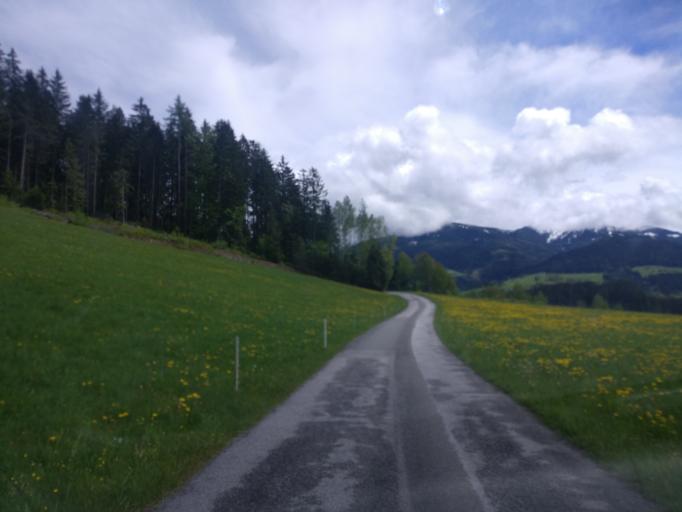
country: AT
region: Salzburg
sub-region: Politischer Bezirk Sankt Johann im Pongau
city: Bischofshofen
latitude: 47.4396
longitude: 13.2286
